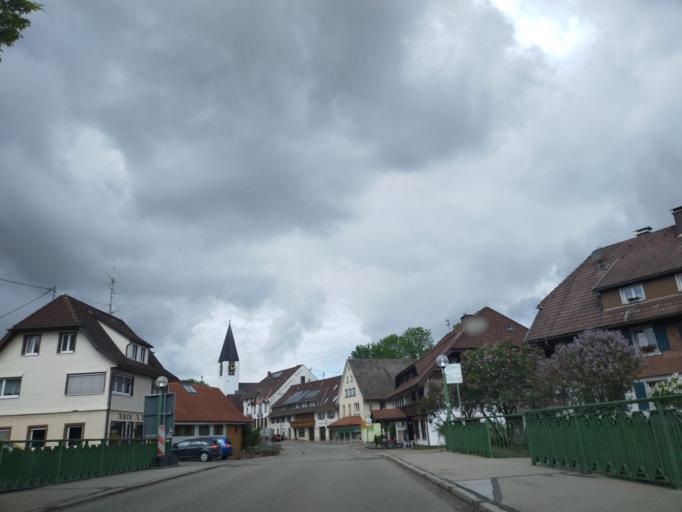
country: DE
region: Baden-Wuerttemberg
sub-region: Freiburg Region
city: Friedenweiler
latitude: 47.8924
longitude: 8.2948
